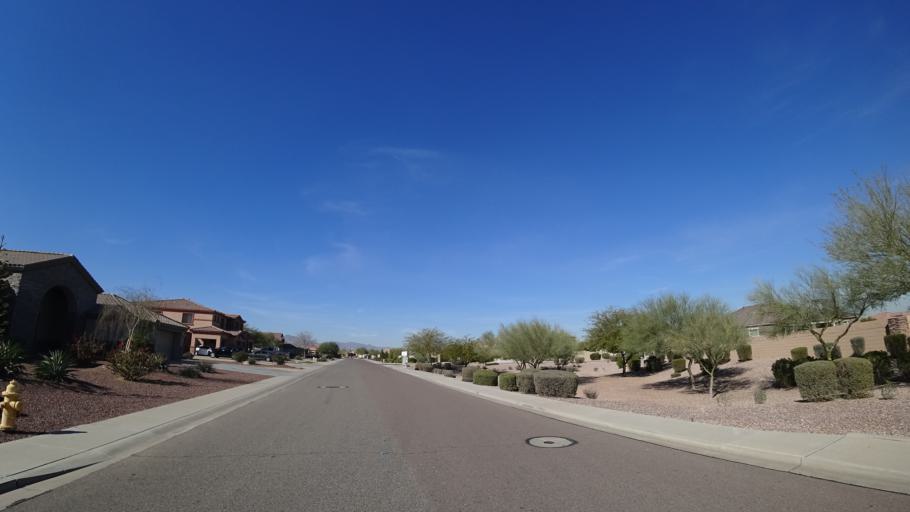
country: US
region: Arizona
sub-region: Maricopa County
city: Citrus Park
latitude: 33.5165
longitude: -112.4561
